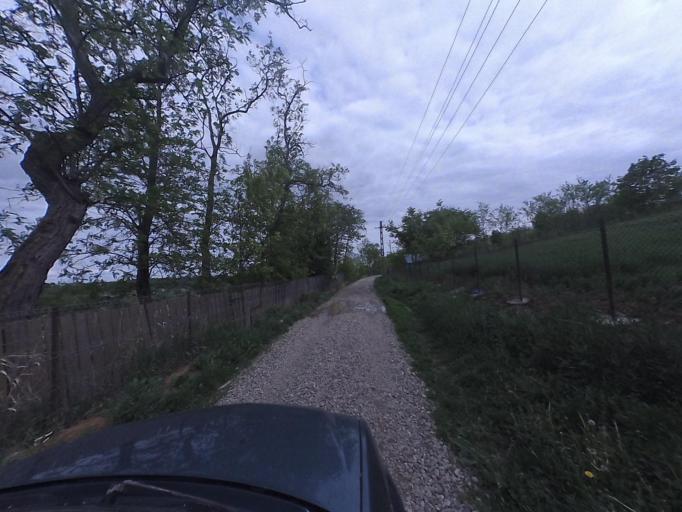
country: RO
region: Neamt
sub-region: Comuna Dulcesti
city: Dulcesti
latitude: 46.9592
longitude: 26.7860
